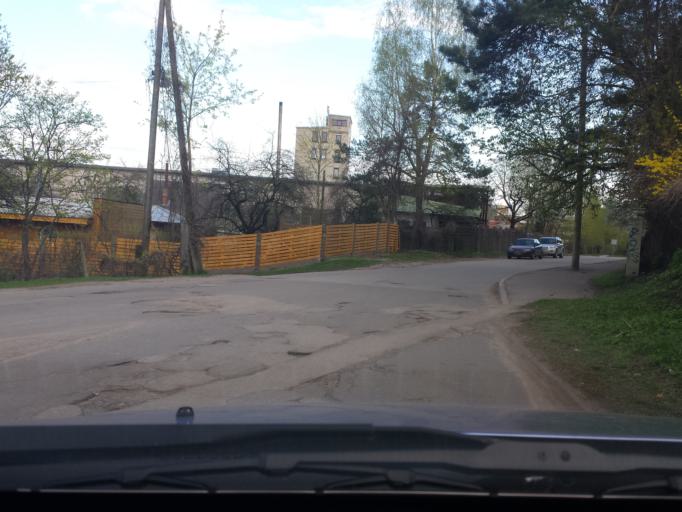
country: LV
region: Riga
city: Jaunciems
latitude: 56.9961
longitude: 24.2254
